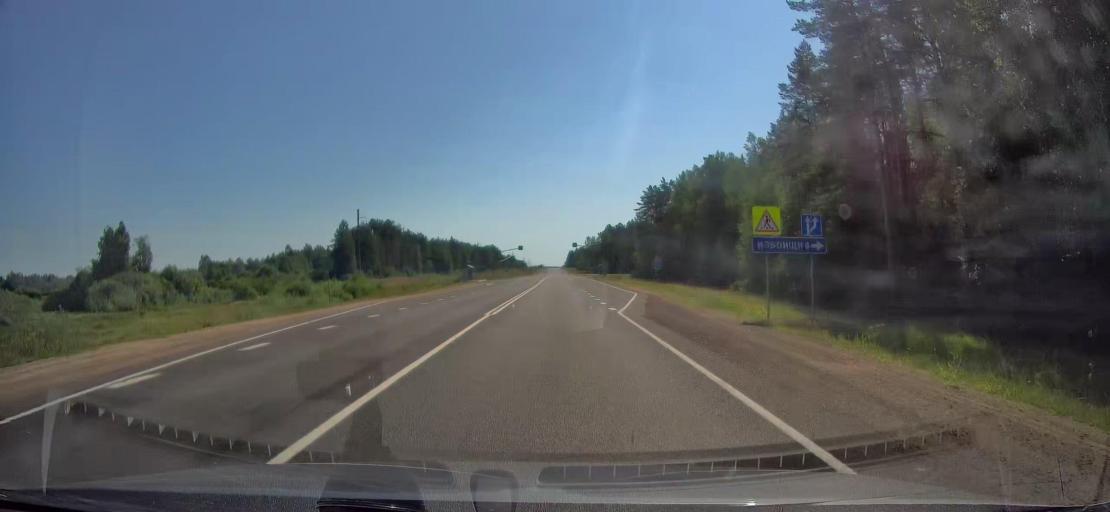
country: RU
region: Vologda
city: Chagoda
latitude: 59.0135
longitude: 35.4248
